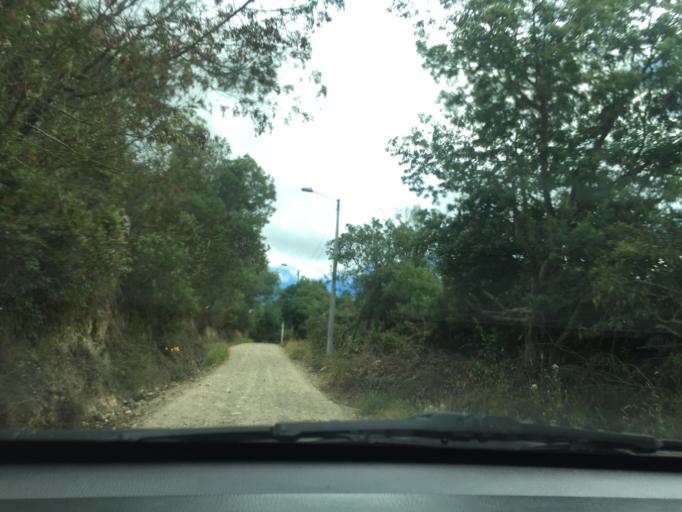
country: CO
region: Cundinamarca
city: Tocancipa
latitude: 4.9617
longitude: -73.8943
